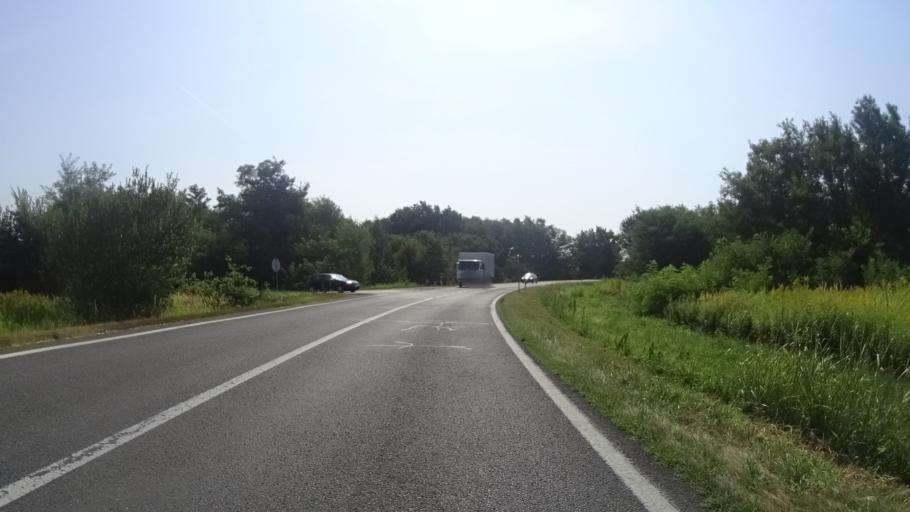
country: HR
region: Medimurska
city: Palovec
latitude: 46.3869
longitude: 16.5657
